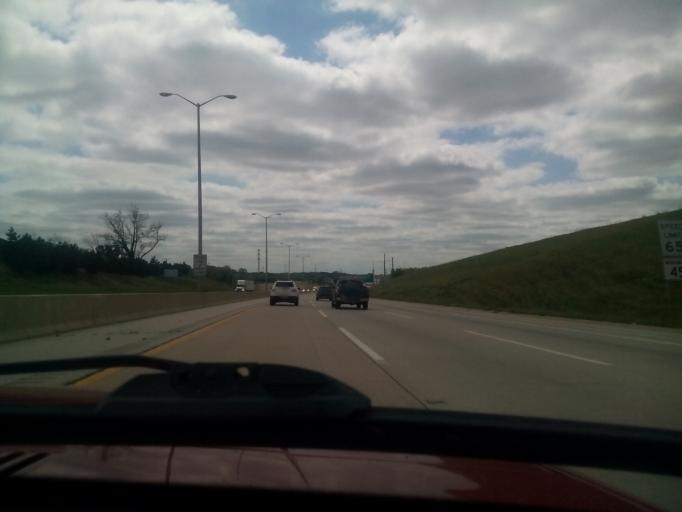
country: US
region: Illinois
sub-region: Cook County
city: Lemont
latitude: 41.6504
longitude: -88.0147
